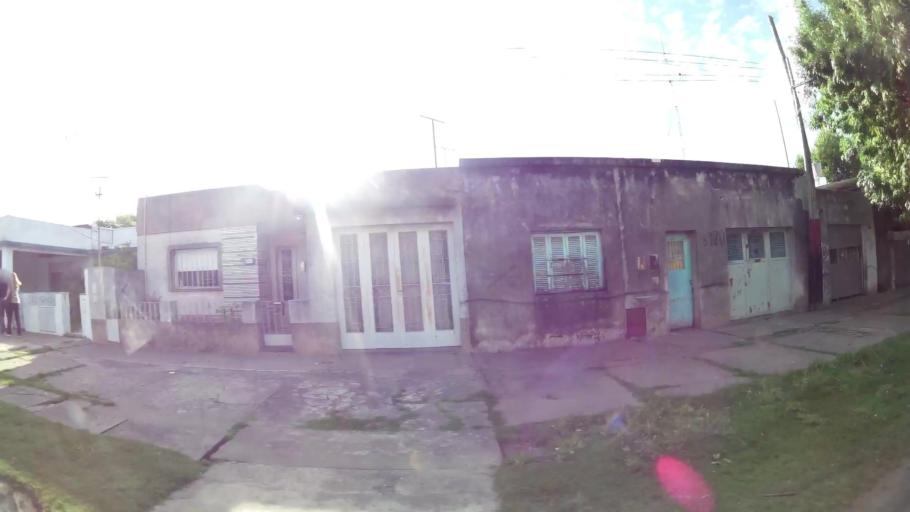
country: AR
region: Santa Fe
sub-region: Departamento de Rosario
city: Rosario
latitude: -32.9783
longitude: -60.6734
